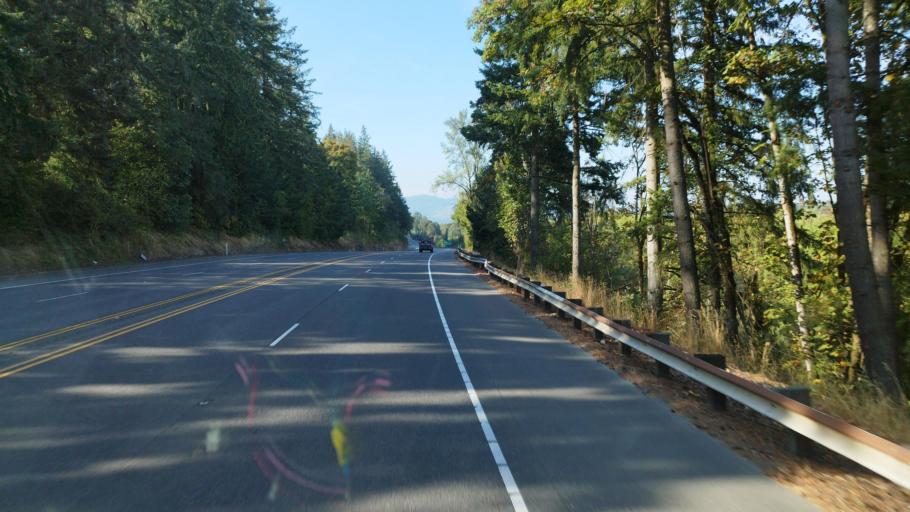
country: US
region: Oregon
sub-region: Washington County
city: Bethany
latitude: 45.6389
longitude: -122.8331
